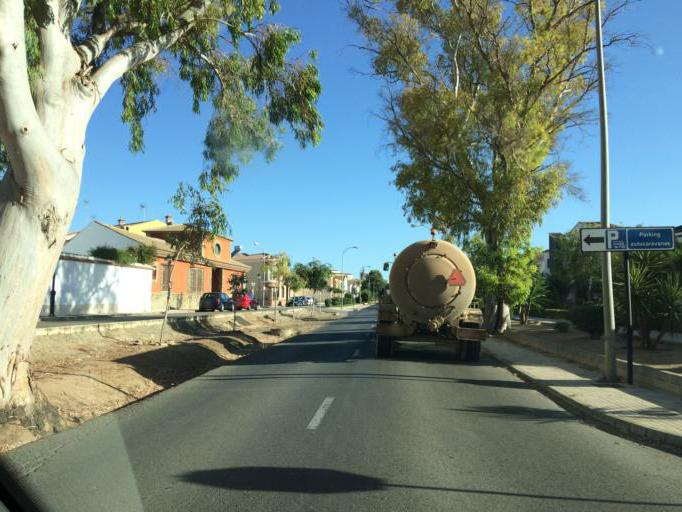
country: ES
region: Andalusia
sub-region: Provincia de Malaga
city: Campillos
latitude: 37.0413
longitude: -4.8595
